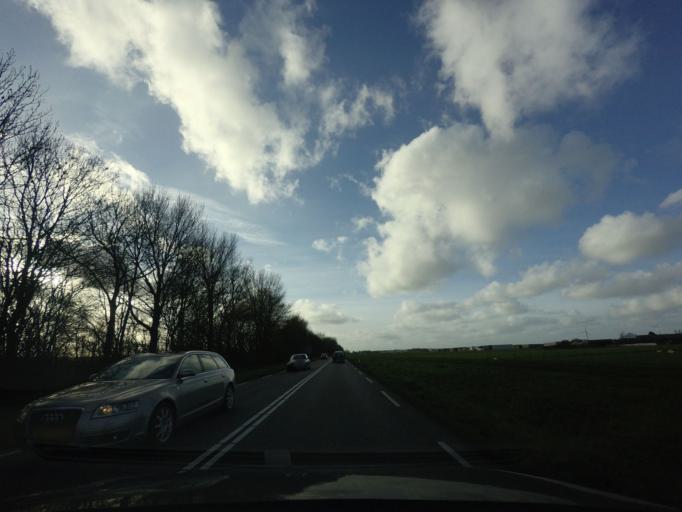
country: NL
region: North Holland
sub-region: Gemeente Langedijk
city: Broek op Langedijk
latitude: 52.7031
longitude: 4.7934
